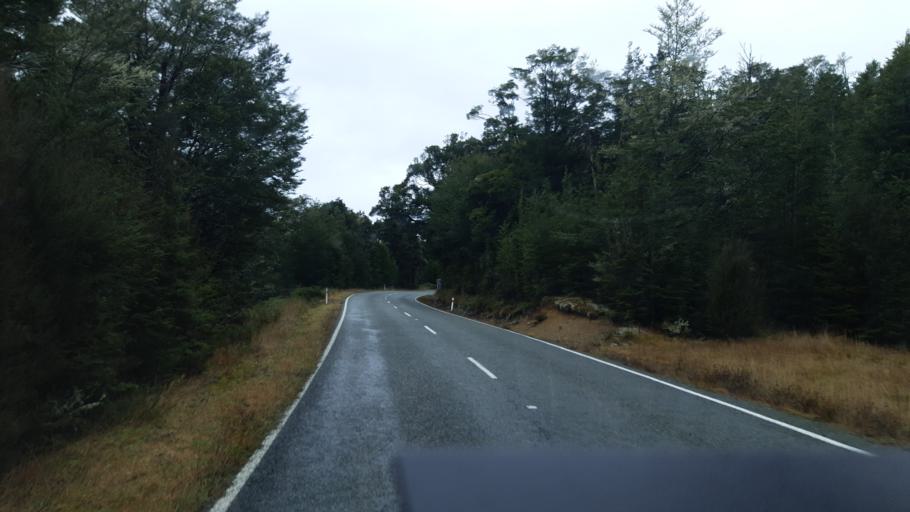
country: NZ
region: Tasman
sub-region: Tasman District
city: Wakefield
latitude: -41.7626
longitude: 172.8970
